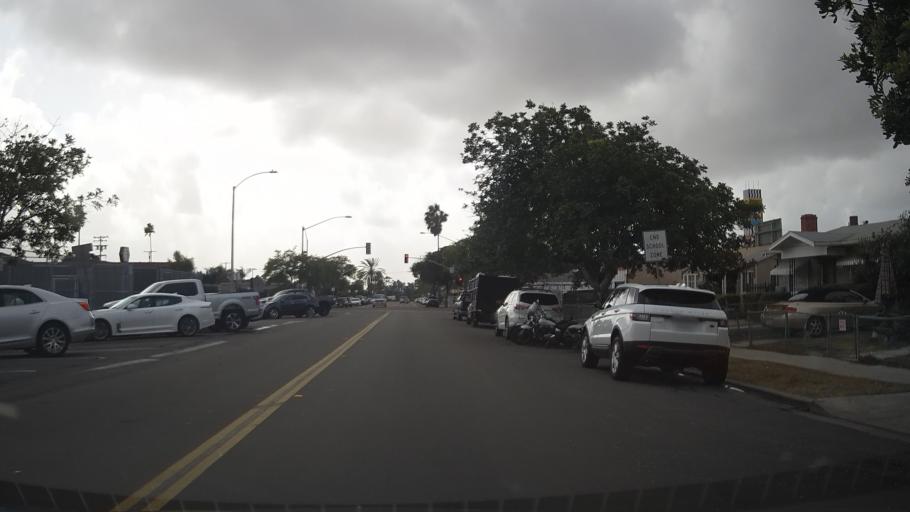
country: US
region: California
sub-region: San Diego County
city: San Diego
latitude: 32.7507
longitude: -117.1181
